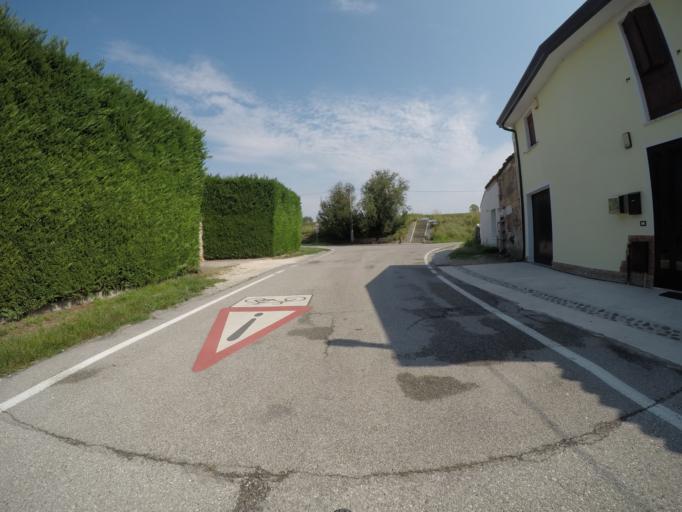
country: IT
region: Veneto
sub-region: Provincia di Rovigo
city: Lendinara
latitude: 45.1140
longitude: 11.6006
